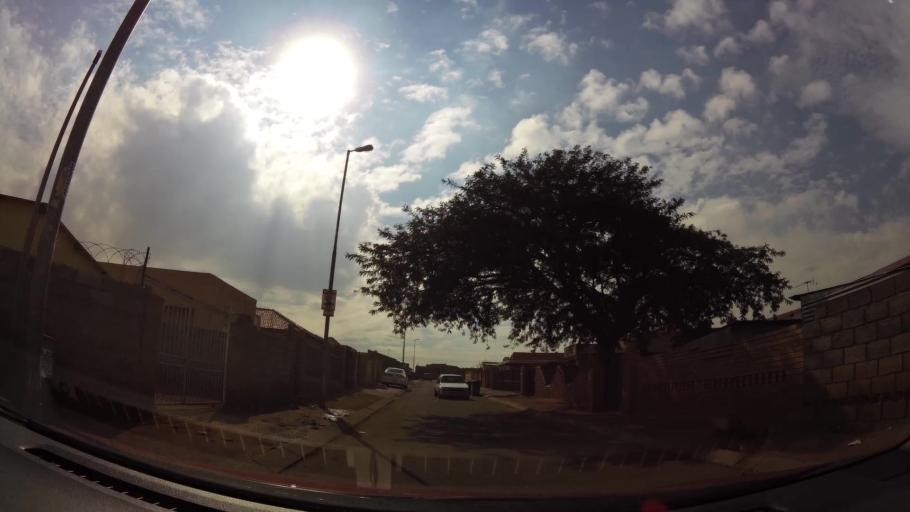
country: ZA
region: Gauteng
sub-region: City of Johannesburg Metropolitan Municipality
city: Soweto
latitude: -26.2577
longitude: 27.8181
